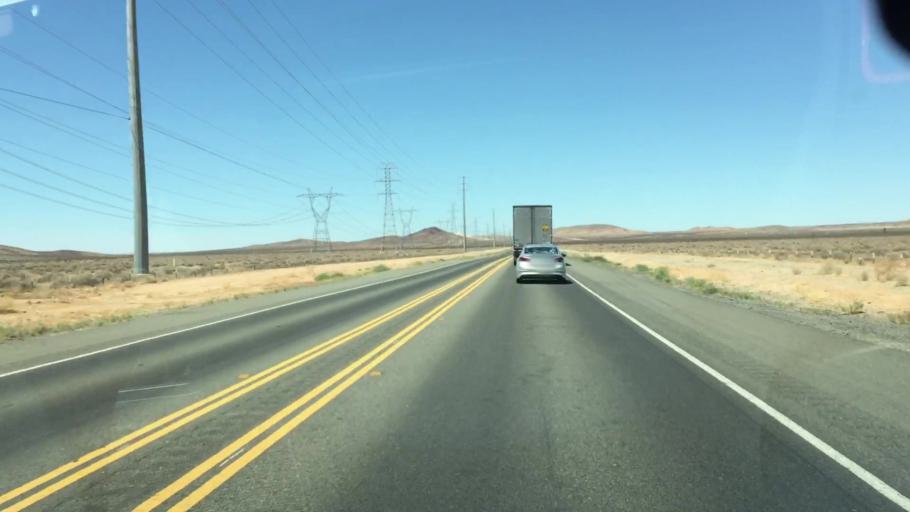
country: US
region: California
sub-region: Kern County
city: Boron
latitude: 34.8292
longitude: -117.4964
